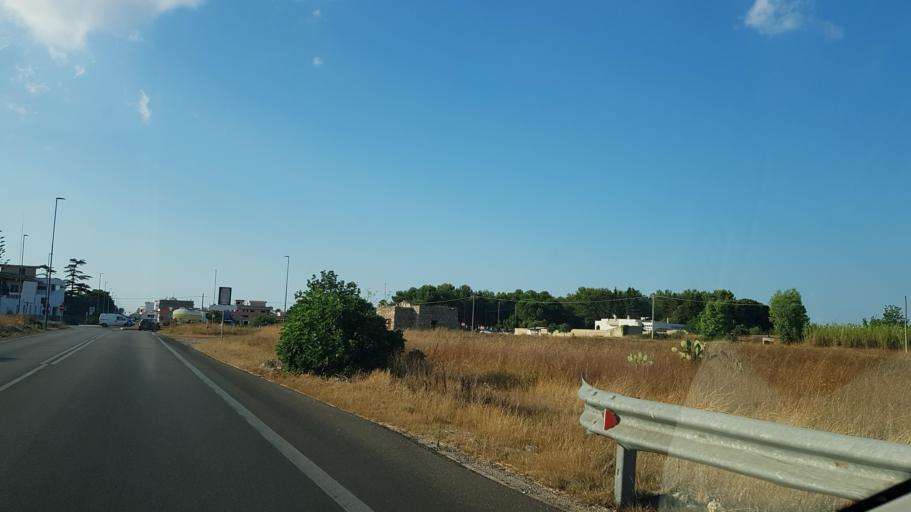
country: IT
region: Apulia
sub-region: Provincia di Lecce
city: Montesano Salentino
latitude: 39.9720
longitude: 18.3265
